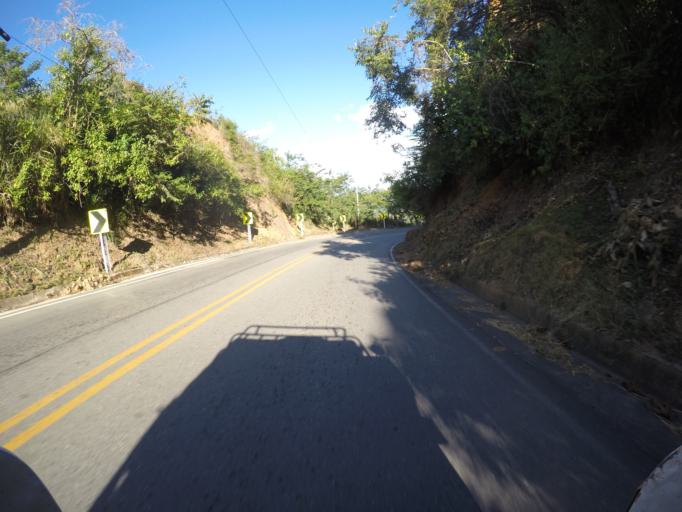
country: CO
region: Valle del Cauca
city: Cartago
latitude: 4.7260
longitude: -75.8610
